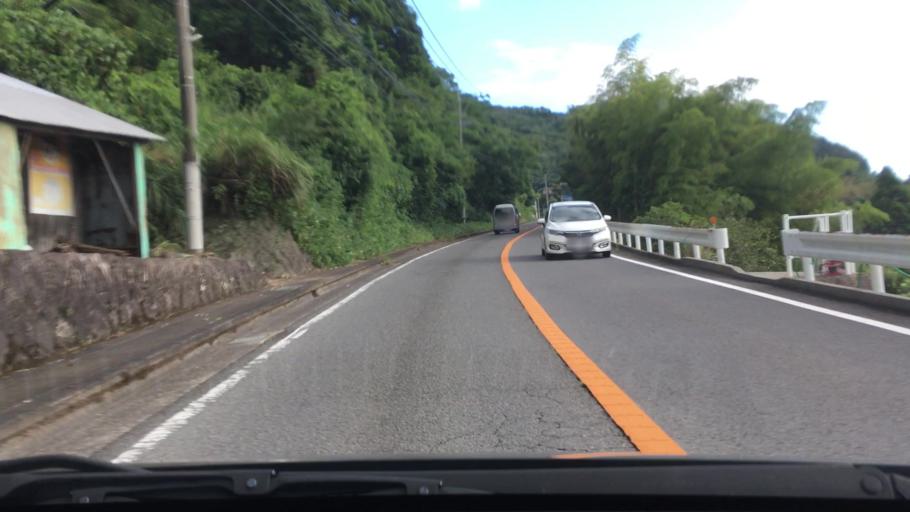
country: JP
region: Nagasaki
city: Togitsu
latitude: 32.8273
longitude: 129.7254
